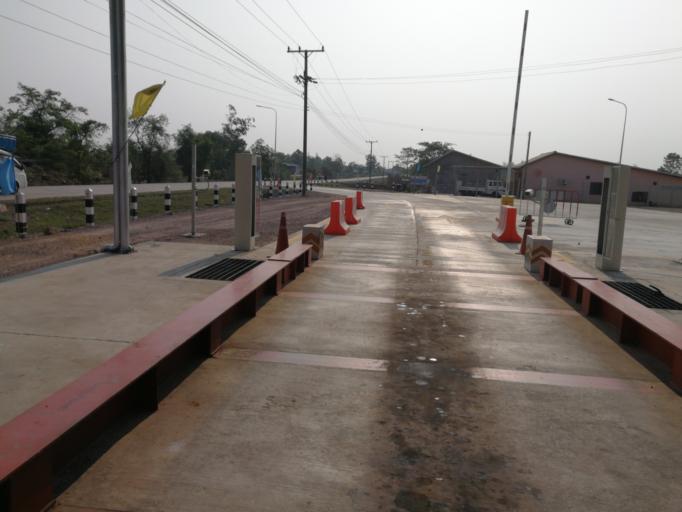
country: TH
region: Mukdahan
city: Wan Yai
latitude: 16.7122
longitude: 105.2508
